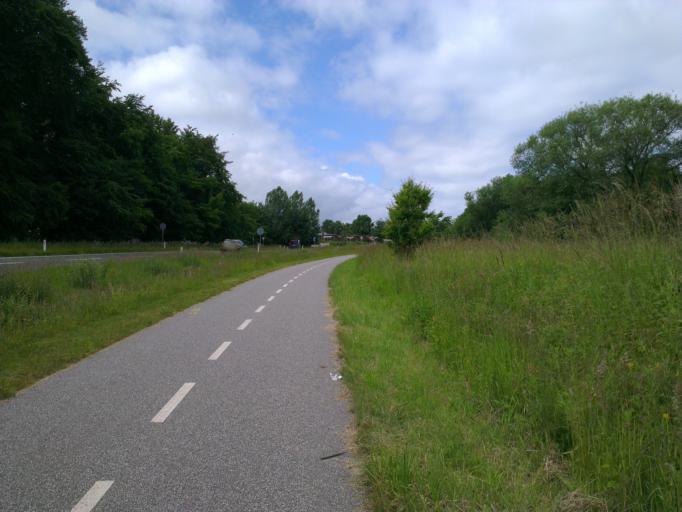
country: DK
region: Zealand
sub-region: Lejre Kommune
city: Lejre
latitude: 55.6498
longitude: 11.9236
